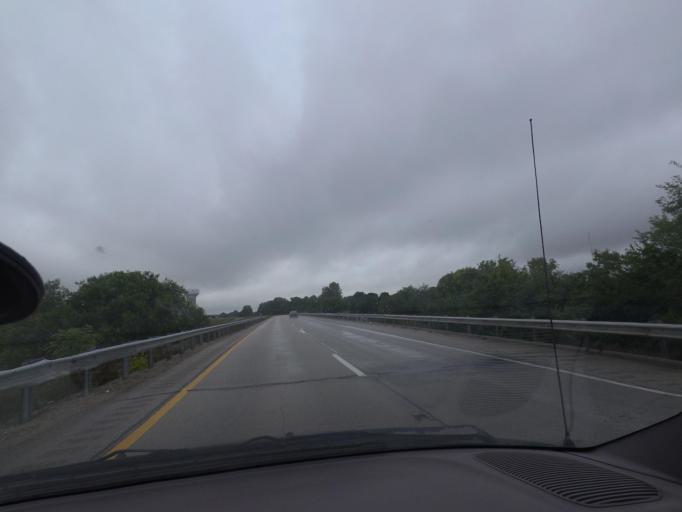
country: US
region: Illinois
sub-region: Champaign County
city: Champaign
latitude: 40.1189
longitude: -88.2869
